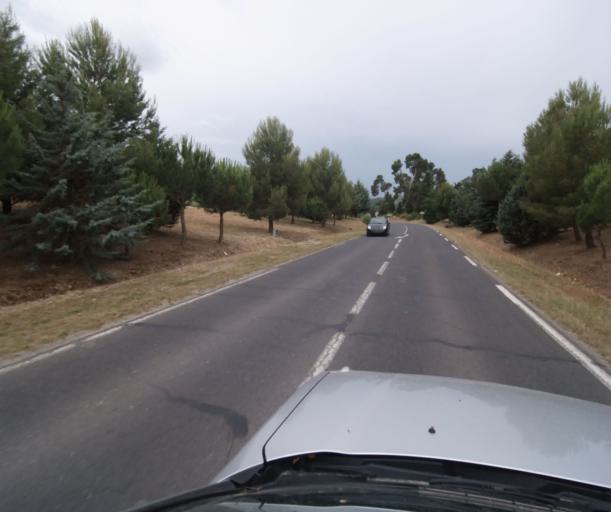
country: FR
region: Languedoc-Roussillon
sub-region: Departement de l'Aude
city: Limoux
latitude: 43.0679
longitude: 2.2273
